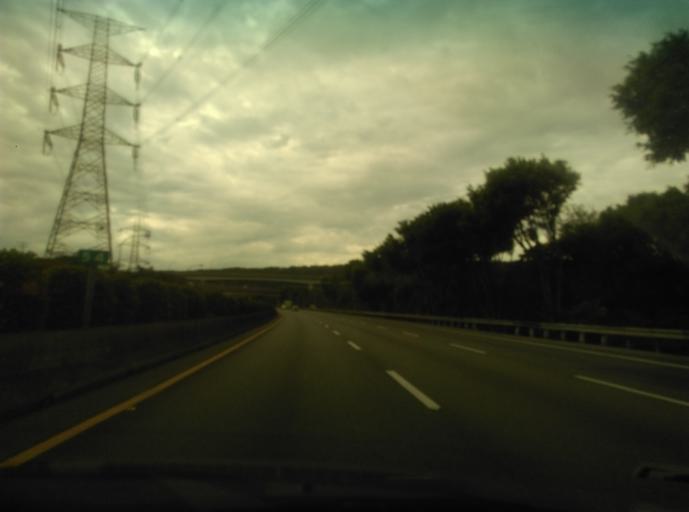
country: TW
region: Taiwan
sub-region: Taoyuan
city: Taoyuan
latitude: 24.9397
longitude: 121.3285
